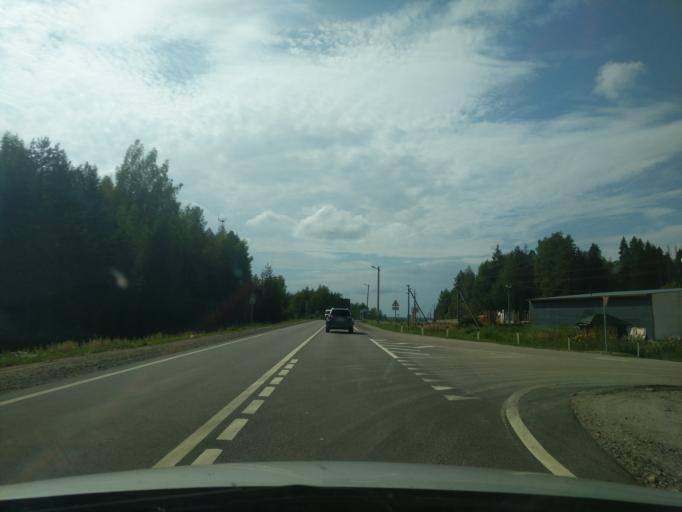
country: RU
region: Kostroma
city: Kadyy
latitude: 57.7999
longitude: 43.2051
